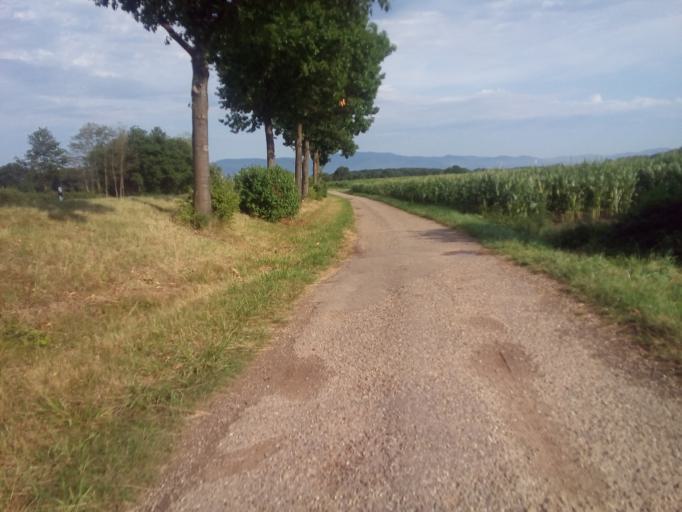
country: DE
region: Baden-Wuerttemberg
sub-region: Karlsruhe Region
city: Schwarzach
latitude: 48.7151
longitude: 8.0354
